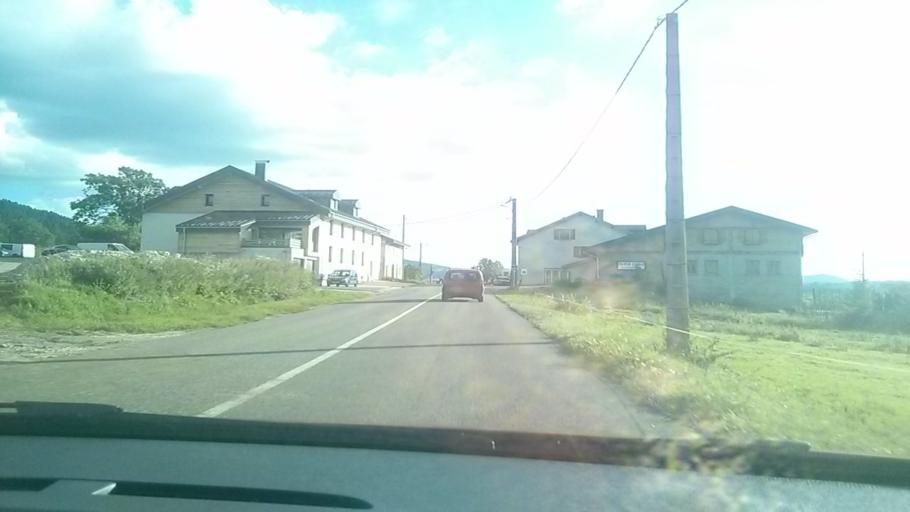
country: FR
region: Franche-Comte
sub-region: Departement du Jura
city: Les Rousses
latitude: 46.5007
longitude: 6.1006
